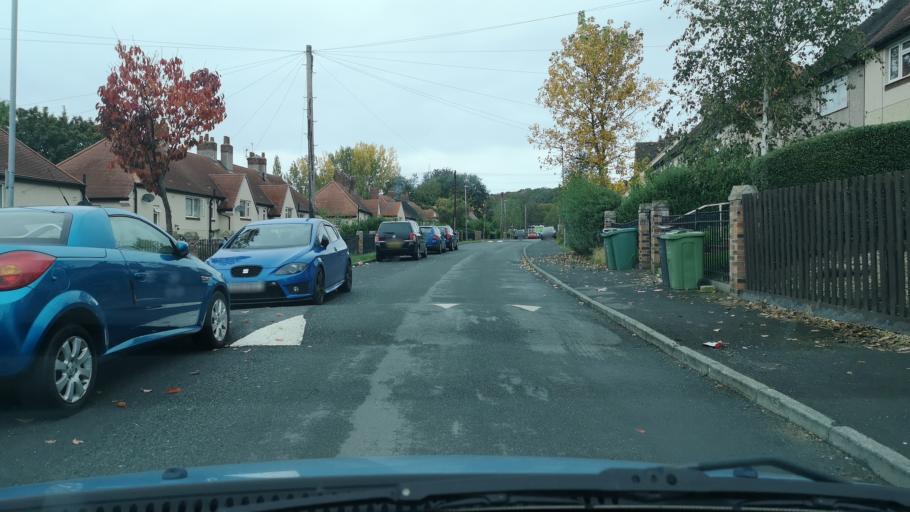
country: GB
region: England
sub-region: City and Borough of Leeds
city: Drighlington
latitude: 53.7348
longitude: -1.6689
